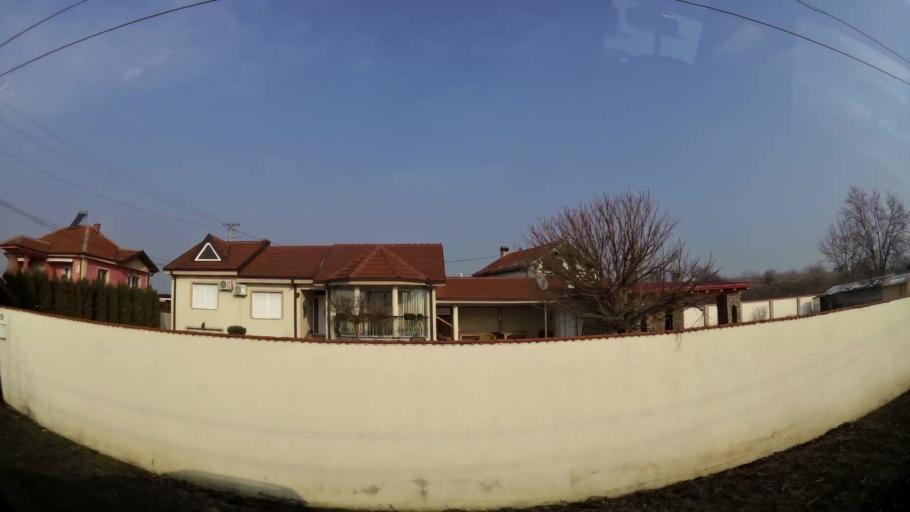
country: MK
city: Kadino
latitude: 41.9805
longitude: 21.5974
